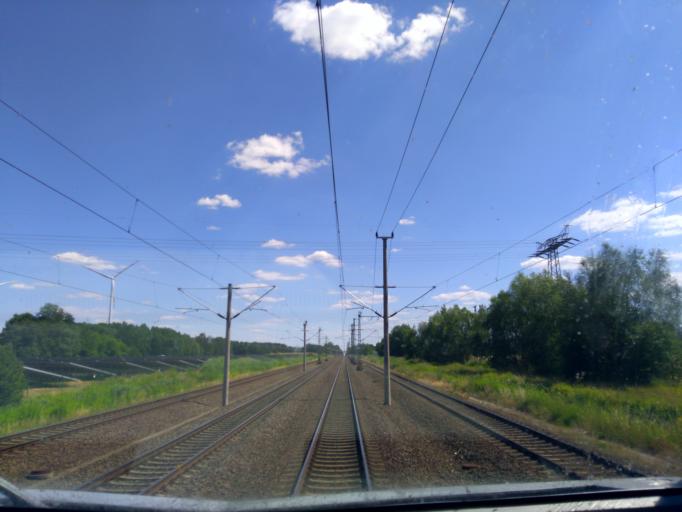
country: DE
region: Brandenburg
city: Wusterhausen
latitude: 52.8490
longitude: 12.4563
